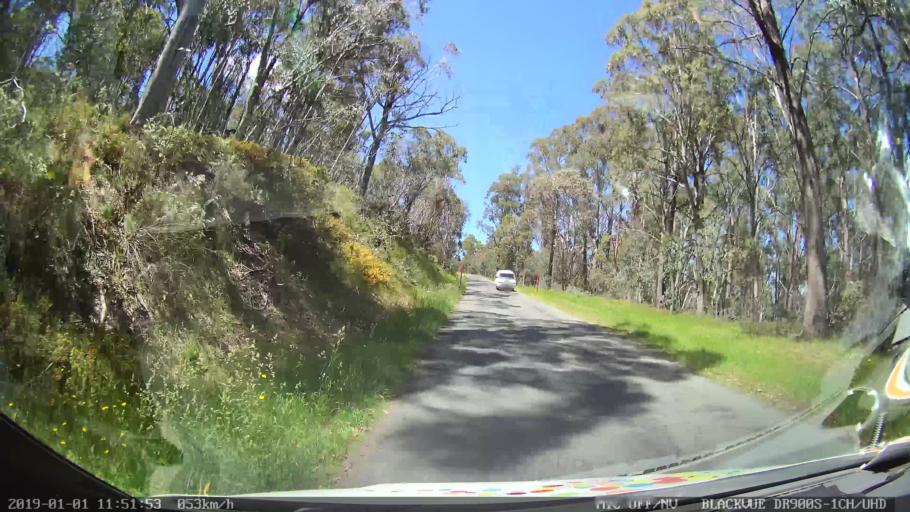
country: AU
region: New South Wales
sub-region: Snowy River
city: Jindabyne
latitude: -35.8857
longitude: 148.4326
